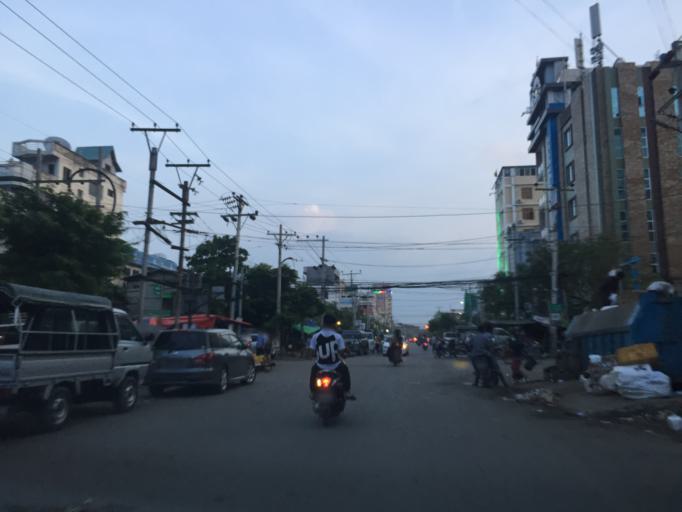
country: MM
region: Mandalay
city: Mandalay
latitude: 21.9709
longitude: 96.0882
